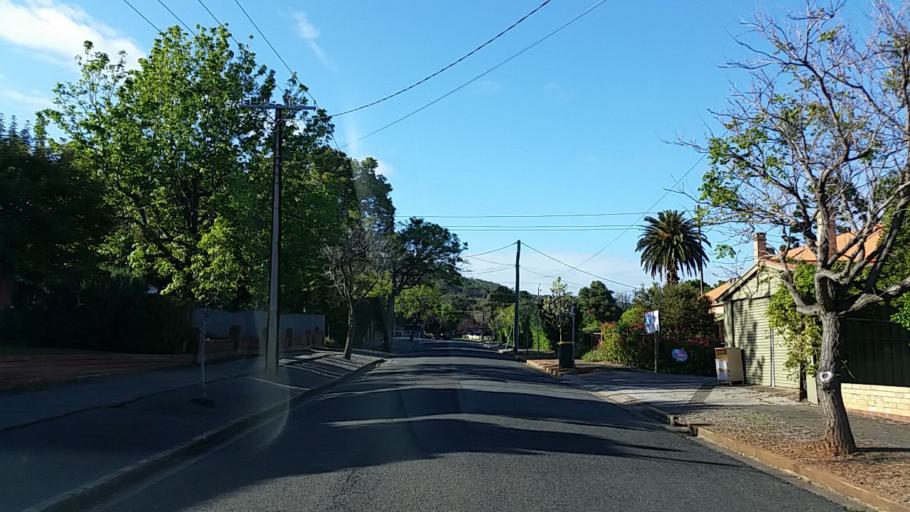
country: AU
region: South Australia
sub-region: Mitcham
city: Clapham
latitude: -34.9892
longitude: 138.6037
